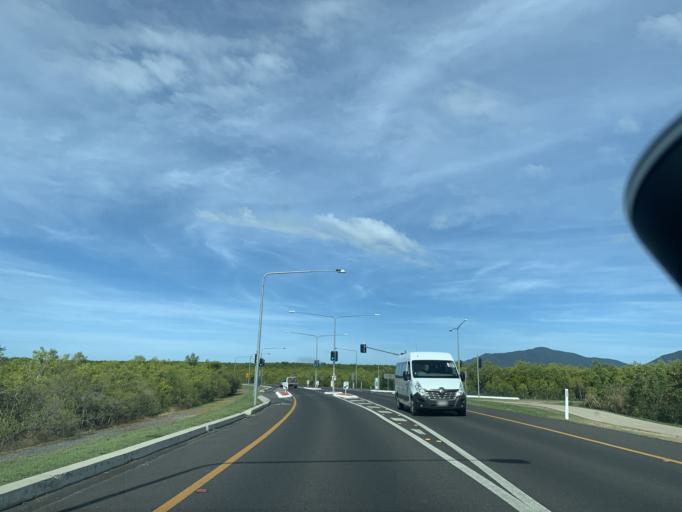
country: AU
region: Queensland
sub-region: Cairns
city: Cairns
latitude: -16.8967
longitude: 145.7572
